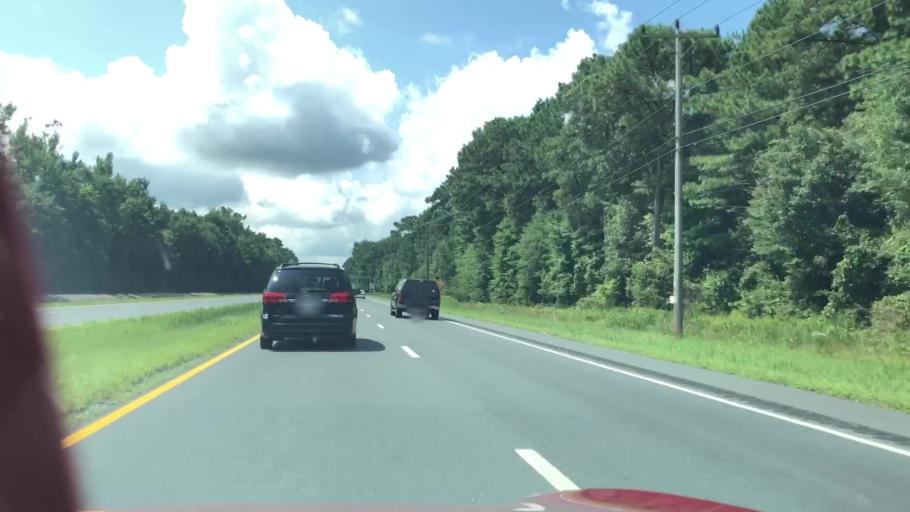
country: US
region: Virginia
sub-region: Accomack County
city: Onancock
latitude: 37.6597
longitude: -75.7362
